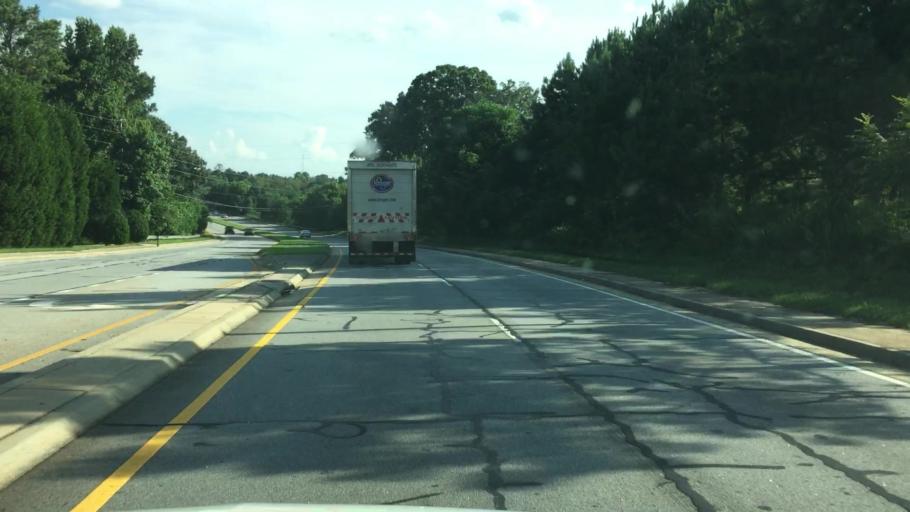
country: US
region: Georgia
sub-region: Gwinnett County
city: Snellville
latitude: 33.7867
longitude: -84.0466
